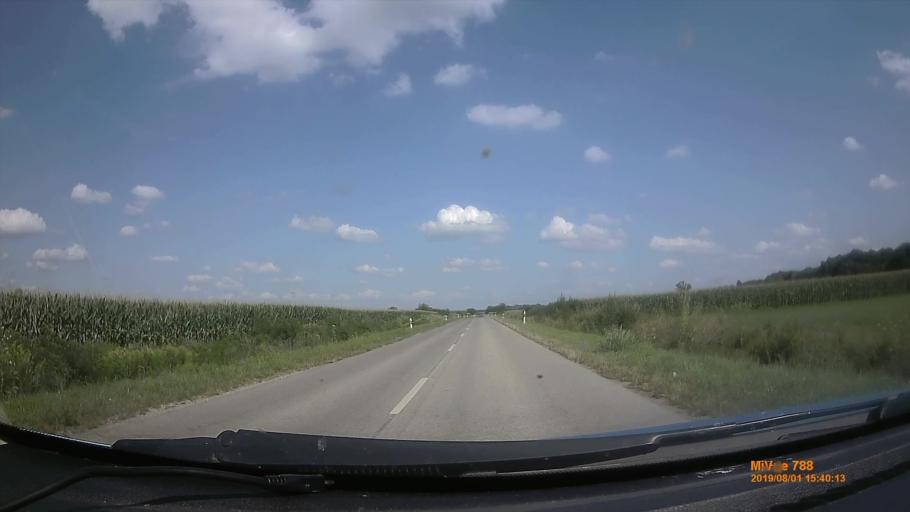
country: HU
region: Baranya
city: Szentlorinc
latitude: 45.9880
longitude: 17.9488
